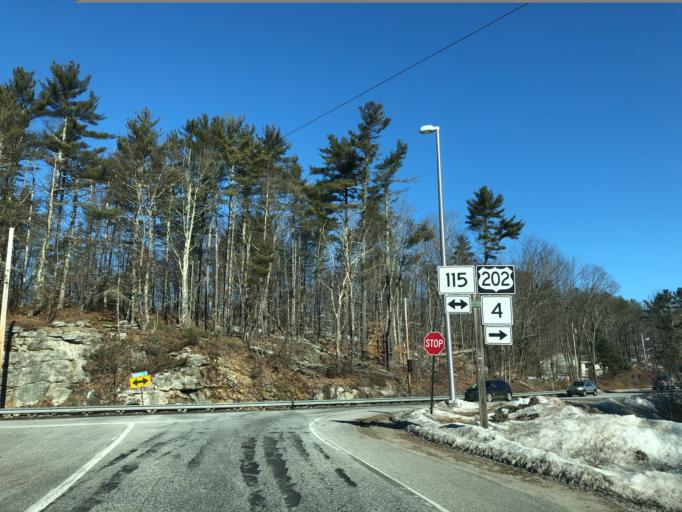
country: US
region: Maine
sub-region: Cumberland County
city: North Windham
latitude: 43.8505
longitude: -70.3842
